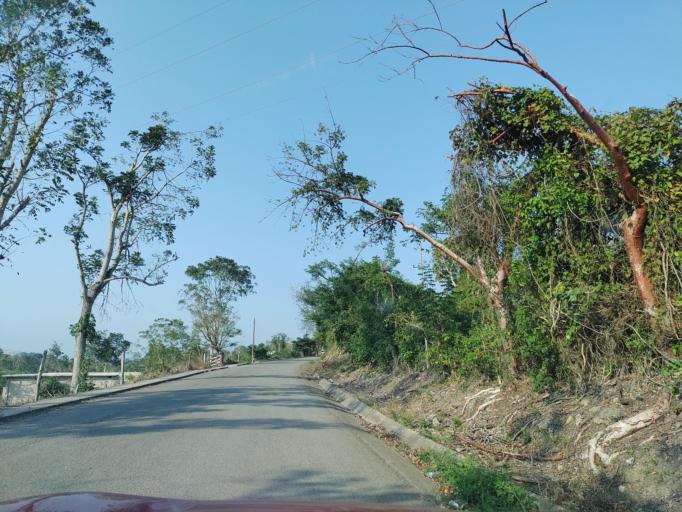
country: MX
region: Veracruz
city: Agua Dulce
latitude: 20.3716
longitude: -97.1841
